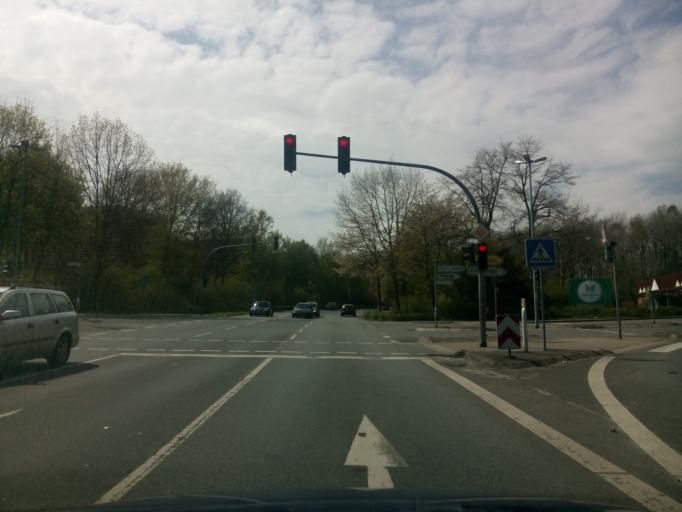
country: DE
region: Lower Saxony
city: Osterholz-Scharmbeck
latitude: 53.2306
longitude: 8.7779
